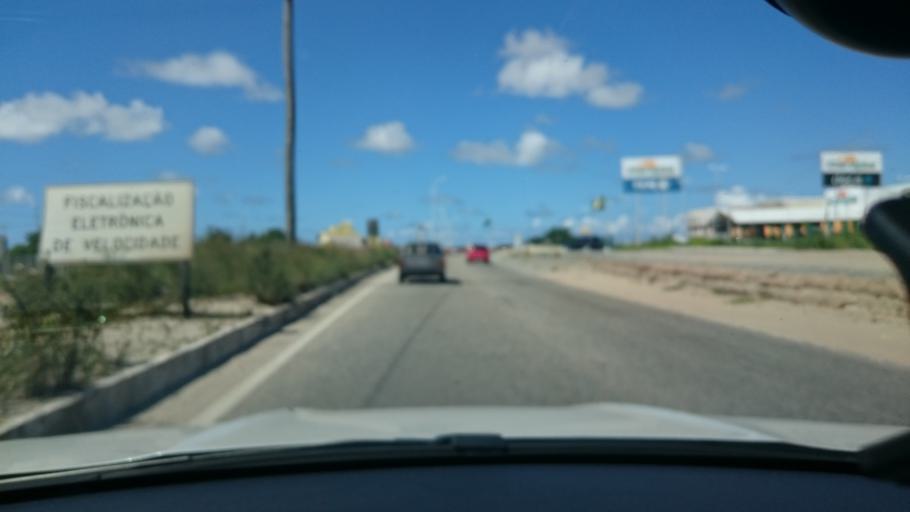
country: BR
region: Paraiba
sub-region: Joao Pessoa
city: Joao Pessoa
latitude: -7.1703
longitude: -34.8718
